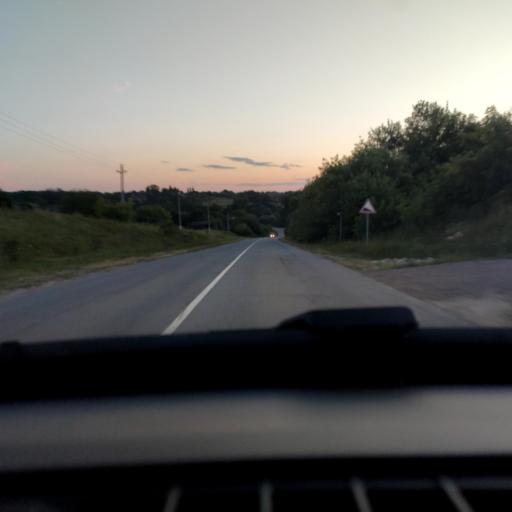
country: RU
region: Lipetsk
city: Zadonsk
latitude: 52.2926
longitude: 38.7684
